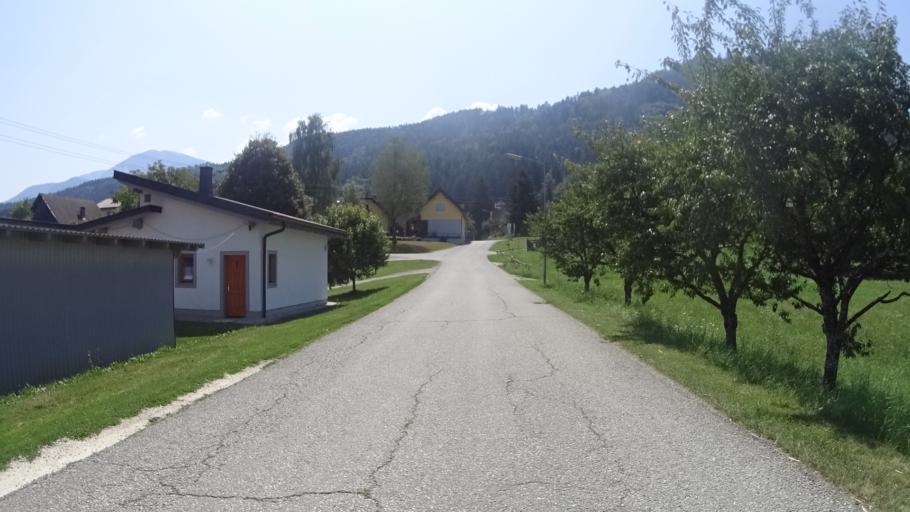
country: AT
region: Carinthia
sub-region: Politischer Bezirk Volkermarkt
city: Globasnitz
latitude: 46.5609
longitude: 14.6705
